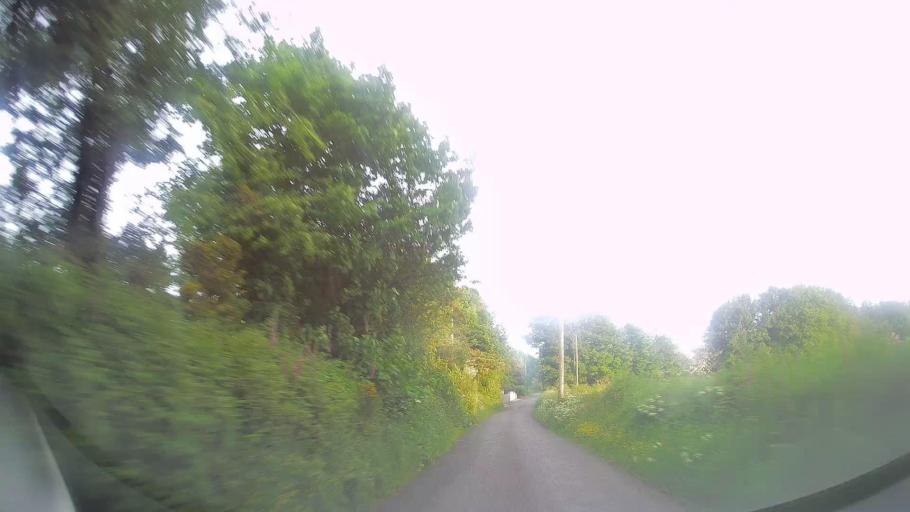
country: IE
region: Munster
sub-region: County Cork
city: Blarney
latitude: 51.9681
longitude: -8.5513
